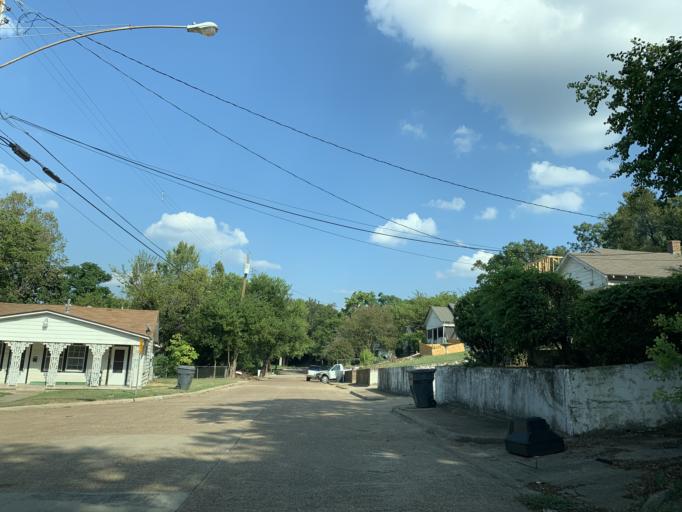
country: US
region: Texas
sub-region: Dallas County
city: Dallas
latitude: 32.7509
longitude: -96.8002
